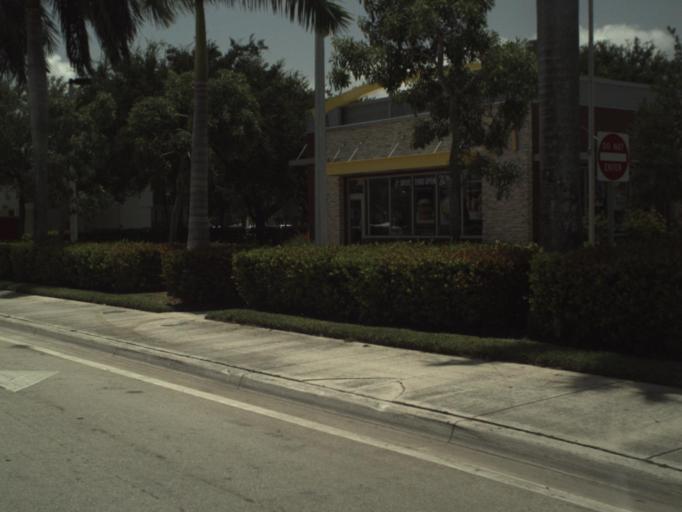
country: US
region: Florida
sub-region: Broward County
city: Coconut Creek
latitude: 26.2307
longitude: -80.1569
